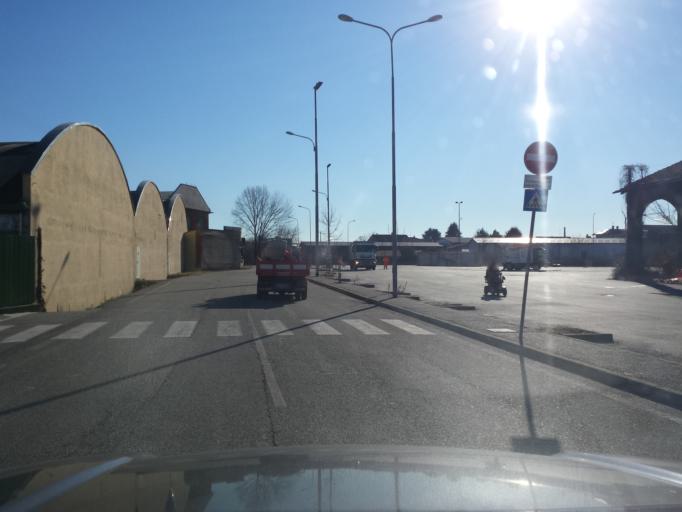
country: IT
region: Piedmont
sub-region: Provincia di Torino
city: Castellamonte
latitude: 45.3803
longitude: 7.7157
